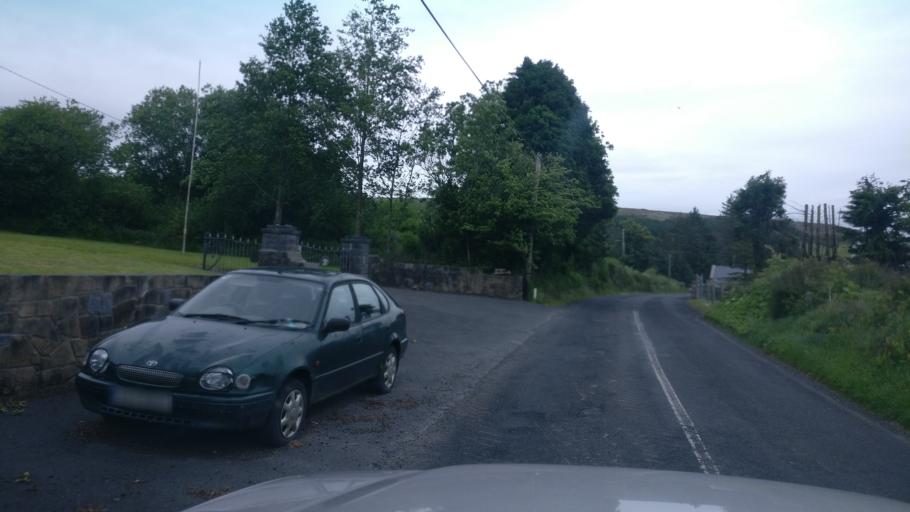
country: IE
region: Connaught
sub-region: County Galway
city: Loughrea
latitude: 53.0576
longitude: -8.6421
